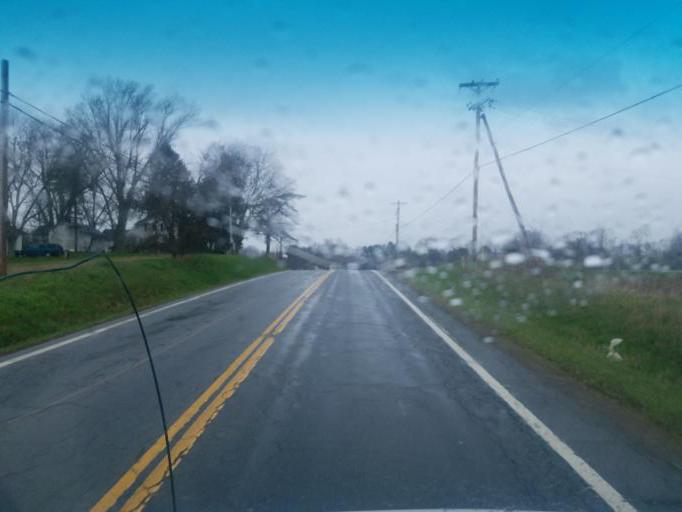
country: US
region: Ohio
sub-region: Wayne County
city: Wooster
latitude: 40.7600
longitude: -81.9313
